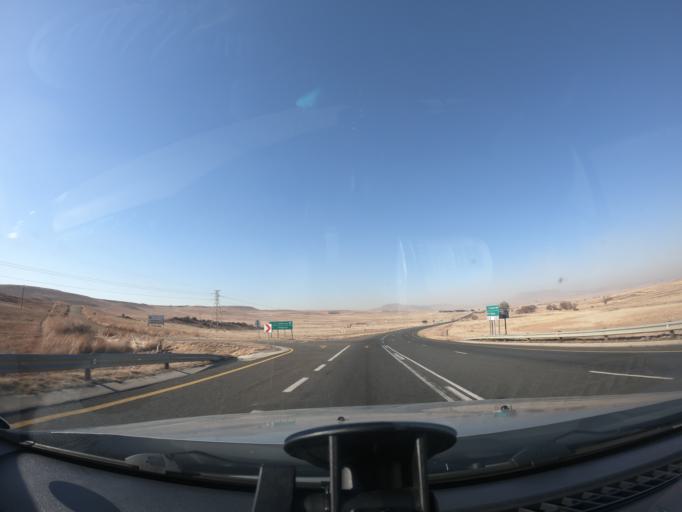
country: ZA
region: Mpumalanga
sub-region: Gert Sibande District Municipality
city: Volksrust
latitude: -27.2161
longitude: 29.8838
